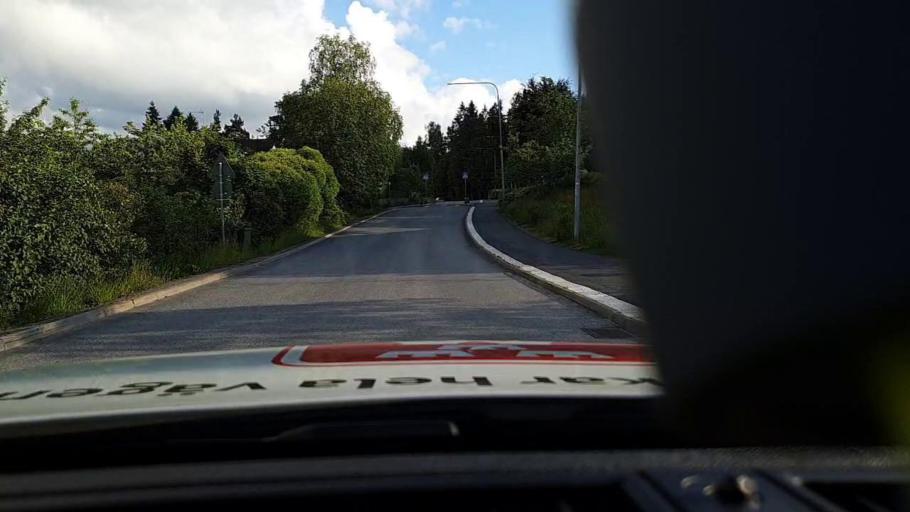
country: SE
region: Stockholm
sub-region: Huddinge Kommun
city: Huddinge
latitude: 59.2497
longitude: 17.9628
